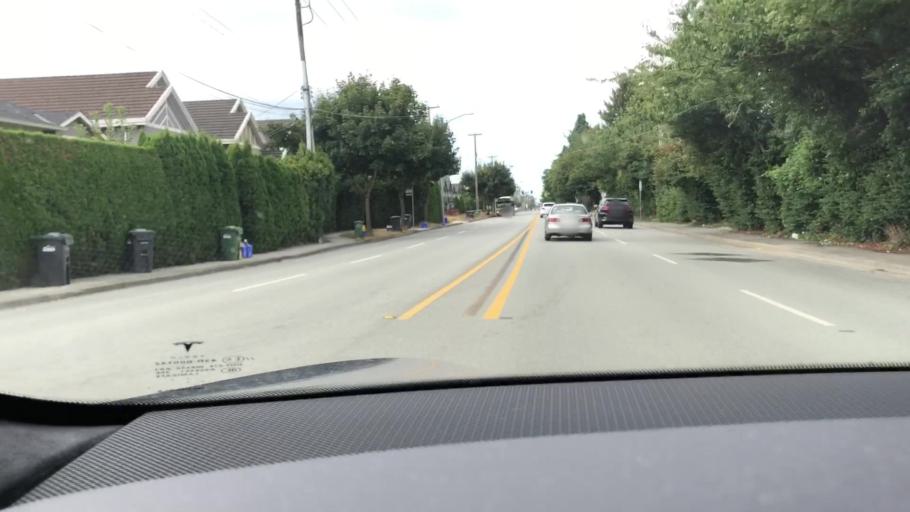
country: CA
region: British Columbia
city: Richmond
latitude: 49.1846
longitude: -123.1100
